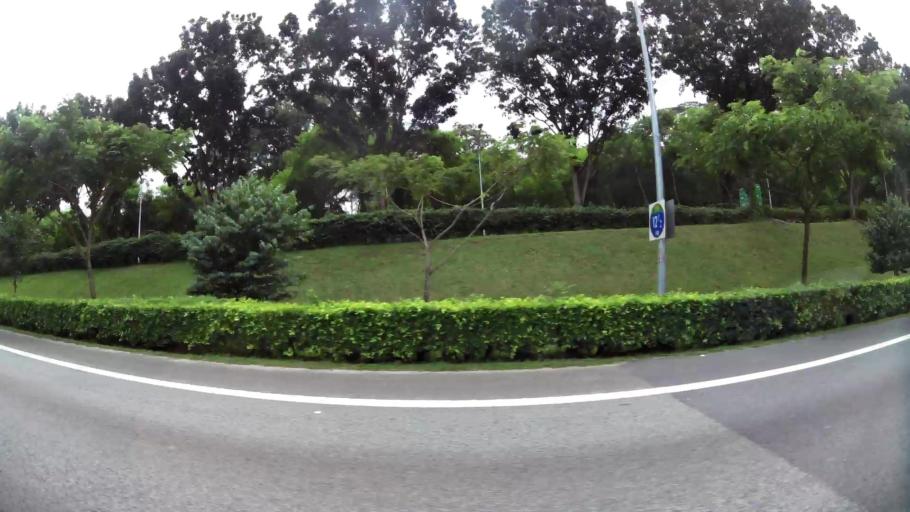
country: MY
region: Johor
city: Kampung Pasir Gudang Baru
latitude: 1.4011
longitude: 103.8739
